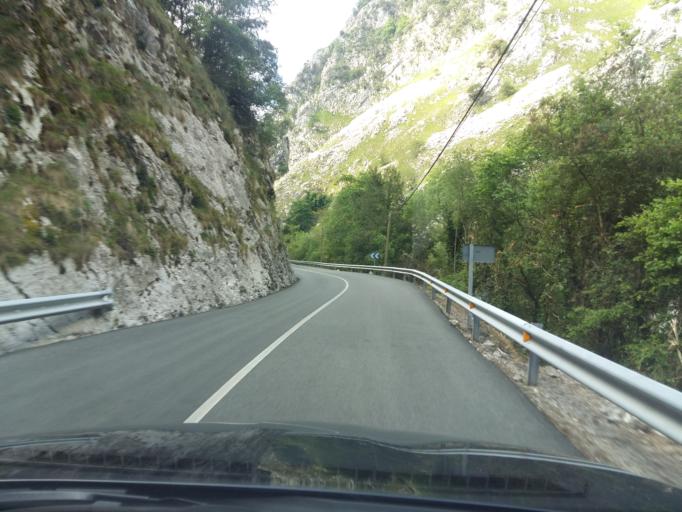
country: ES
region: Cantabria
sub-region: Provincia de Cantabria
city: Tresviso
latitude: 43.3030
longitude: -4.6057
